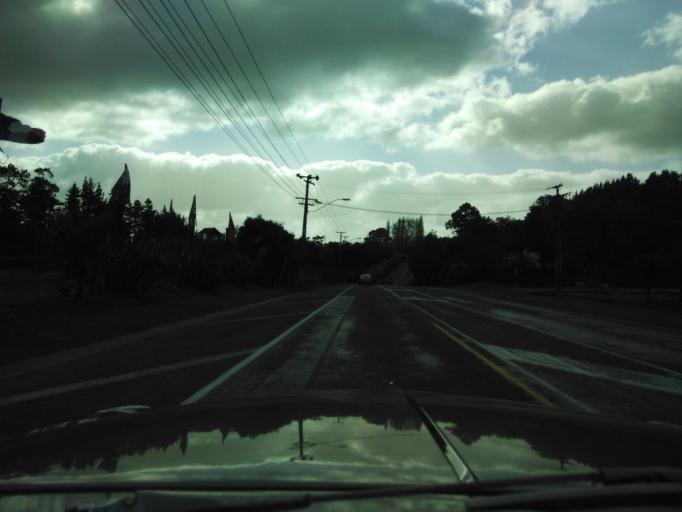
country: NZ
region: Auckland
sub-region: Auckland
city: Wellsford
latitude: -36.2545
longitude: 174.5091
